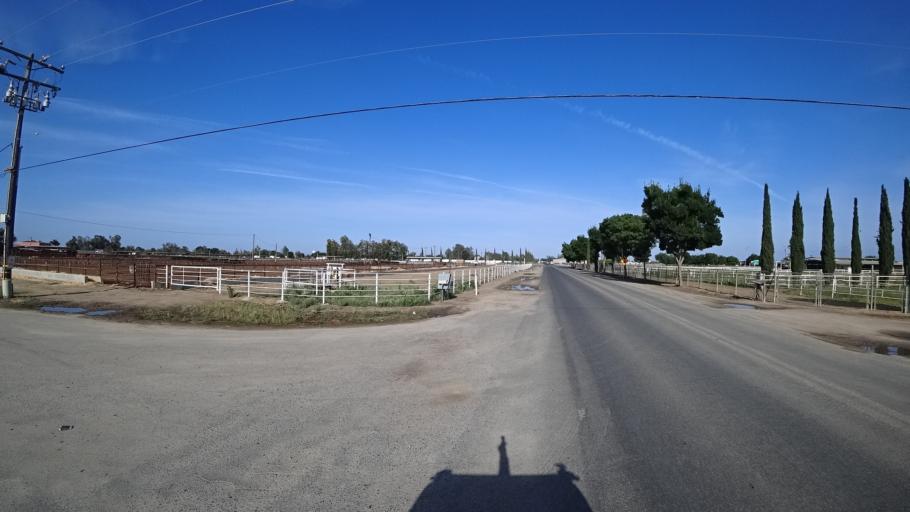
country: US
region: California
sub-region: Kings County
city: Home Garden
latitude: 36.3231
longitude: -119.6168
